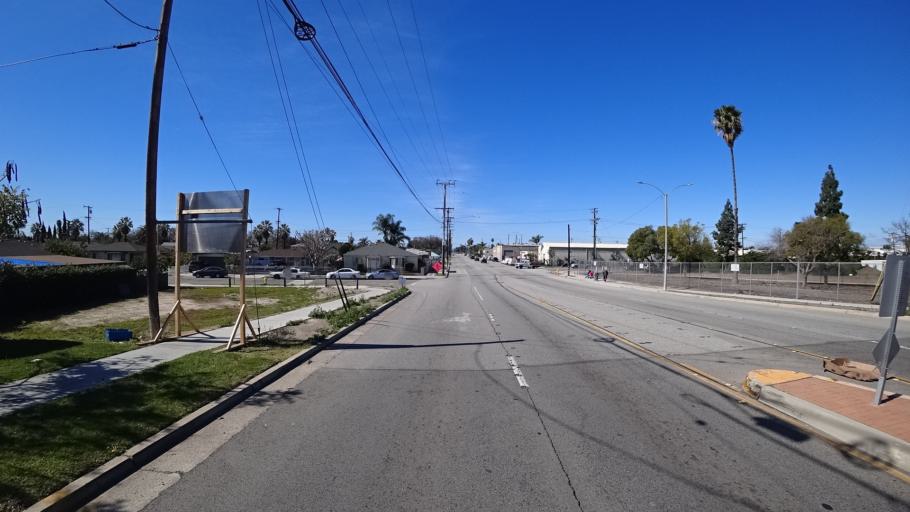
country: US
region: California
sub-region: Orange County
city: Anaheim
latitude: 33.8472
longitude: -117.9102
